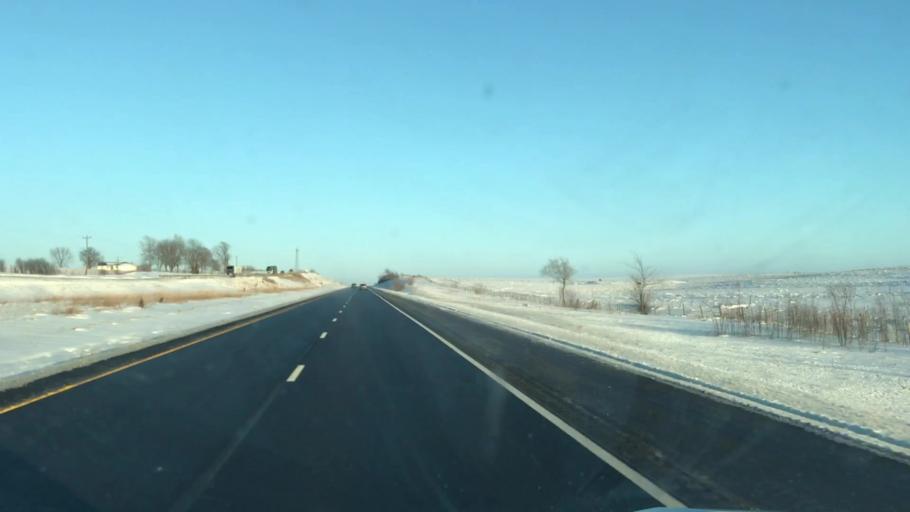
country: US
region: Missouri
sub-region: Clinton County
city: Gower
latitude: 39.7614
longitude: -94.5504
